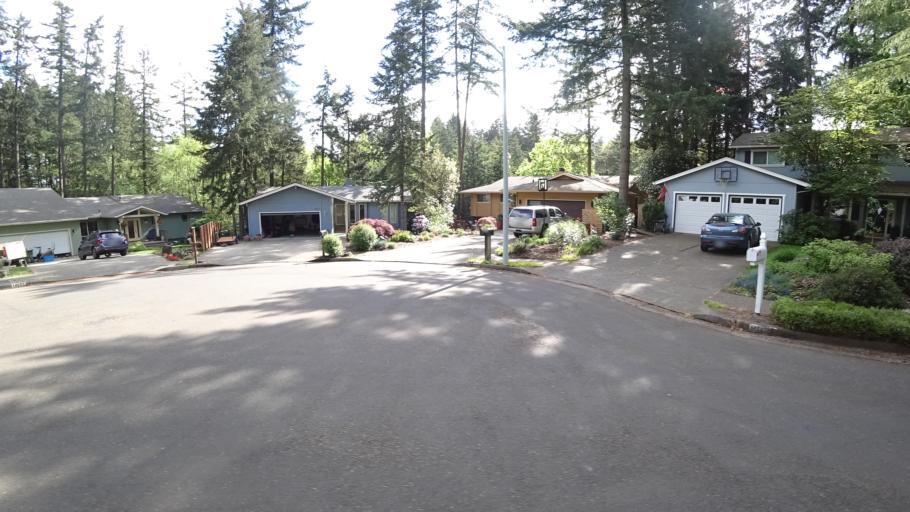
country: US
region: Oregon
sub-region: Washington County
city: Beaverton
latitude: 45.4668
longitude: -122.8271
